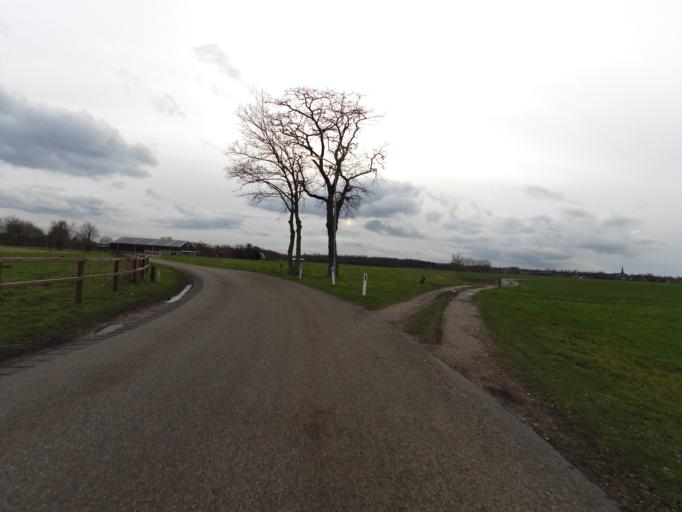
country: NL
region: Gelderland
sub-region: Oude IJsselstreek
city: Wisch
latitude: 51.9398
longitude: 6.3654
